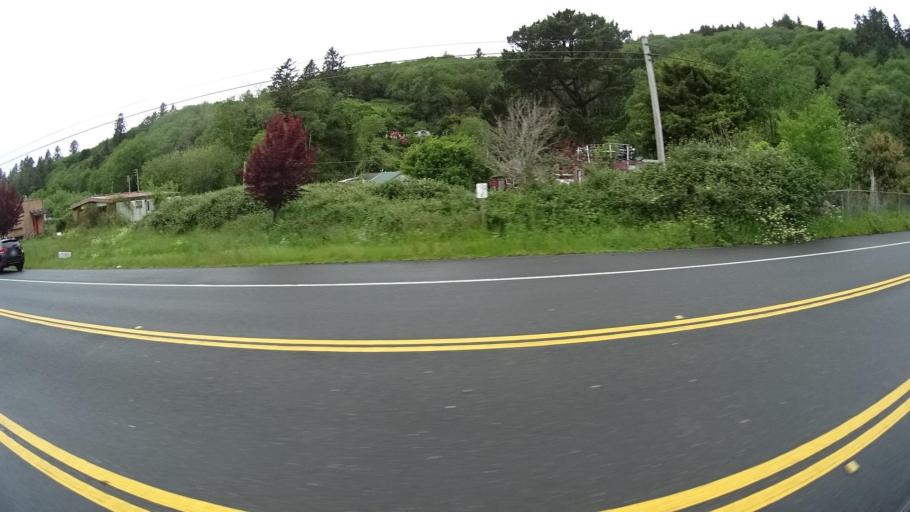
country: US
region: California
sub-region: Humboldt County
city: Westhaven-Moonstone
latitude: 41.2949
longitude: -124.0549
